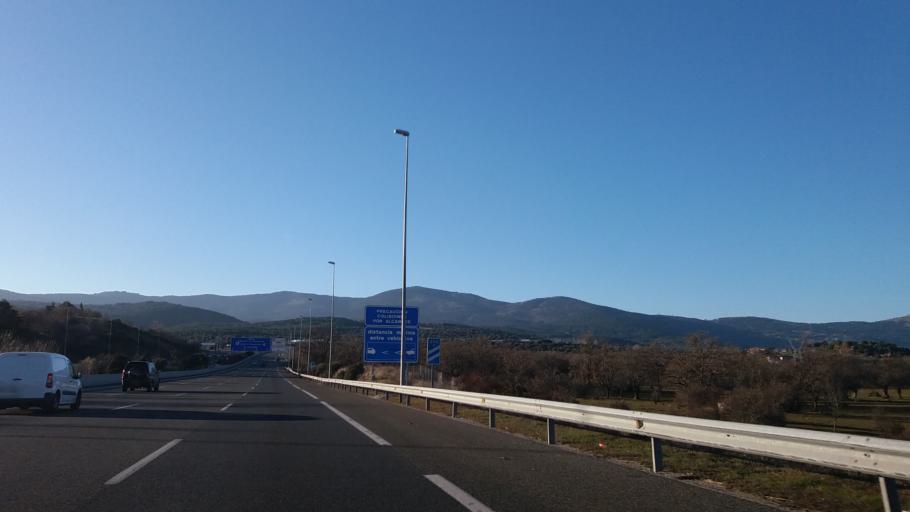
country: ES
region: Madrid
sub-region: Provincia de Madrid
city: Guadarrama
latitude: 40.6548
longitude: -4.0848
